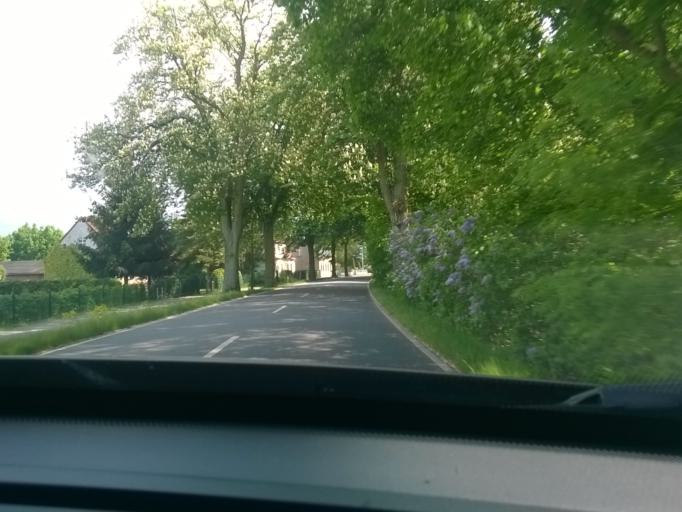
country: DE
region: Brandenburg
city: Wittstock
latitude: 53.1506
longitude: 12.4879
